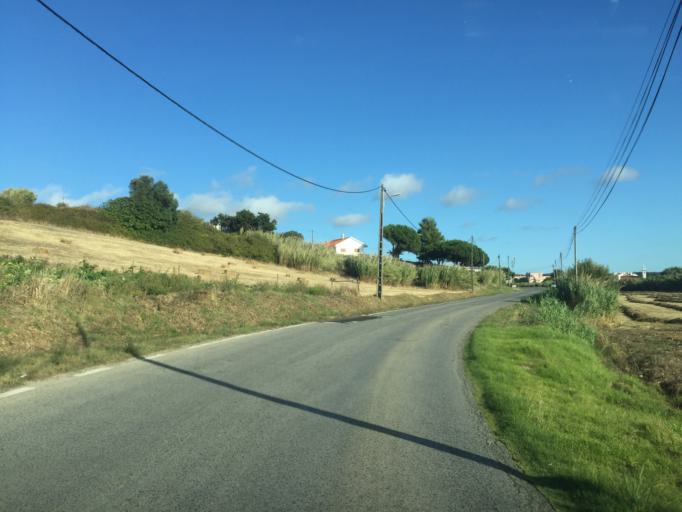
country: PT
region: Lisbon
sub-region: Torres Vedras
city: A dos Cunhados
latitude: 39.1595
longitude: -9.3036
